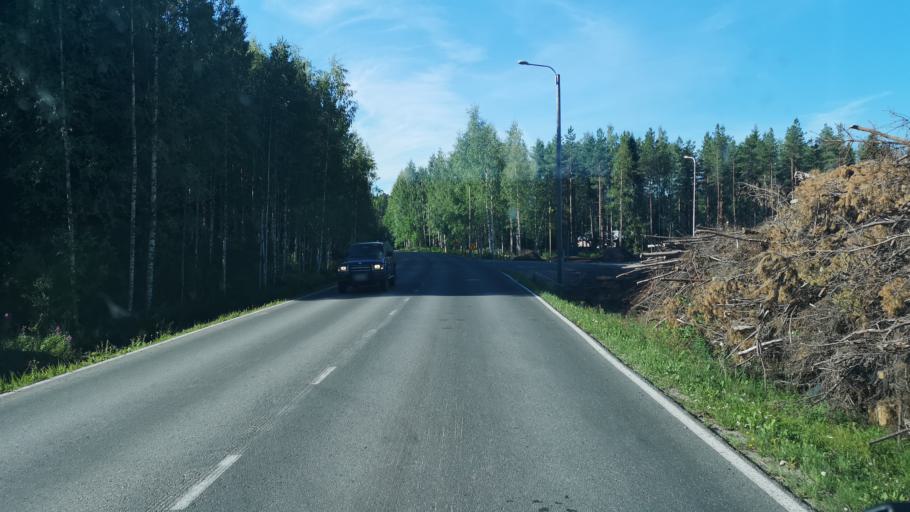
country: FI
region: Southern Ostrobothnia
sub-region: Seinaejoki
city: Lapua
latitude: 62.9717
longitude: 23.0543
